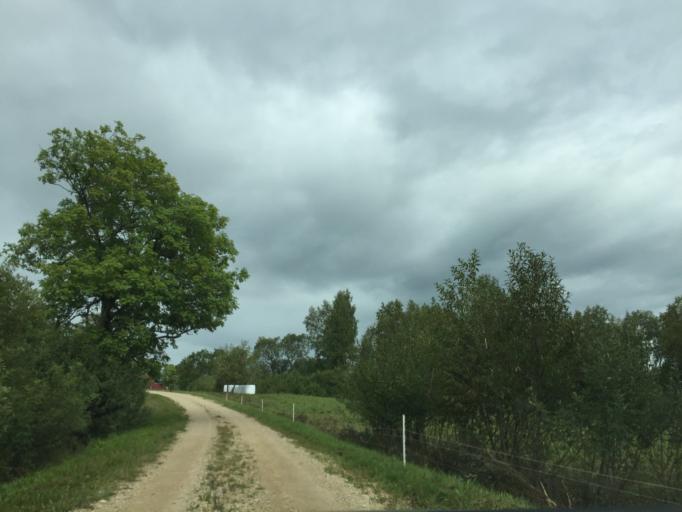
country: LV
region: Pargaujas
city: Stalbe
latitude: 57.5101
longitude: 24.9159
